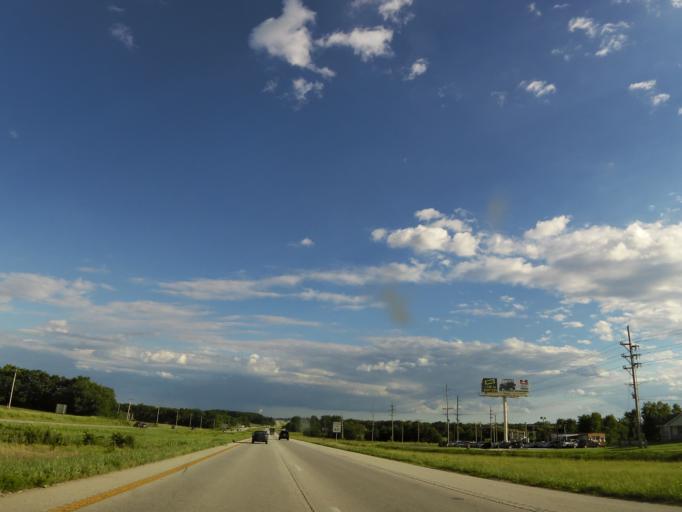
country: US
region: Missouri
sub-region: Lincoln County
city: Moscow Mills
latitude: 38.9383
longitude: -90.9261
